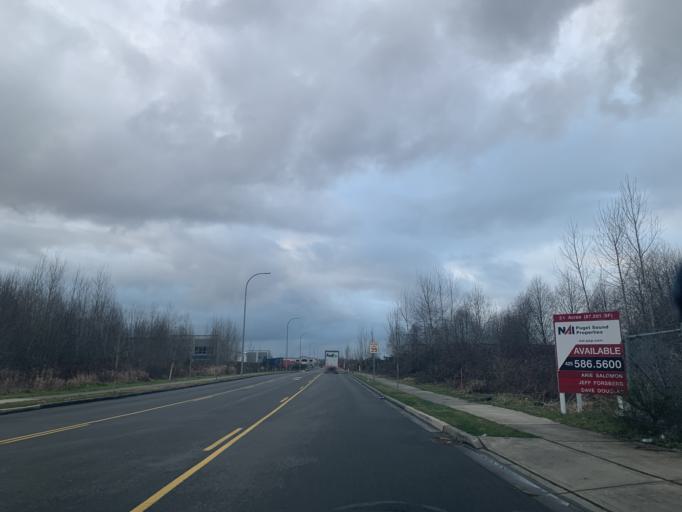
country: US
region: Washington
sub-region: Pierce County
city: Milton
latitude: 47.2336
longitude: -122.3256
